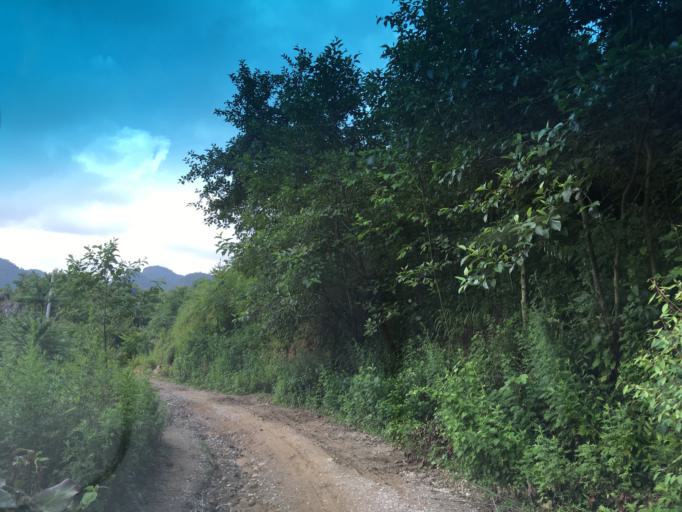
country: CN
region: Guangxi Zhuangzu Zizhiqu
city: Xinzhou
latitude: 24.9898
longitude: 105.6324
